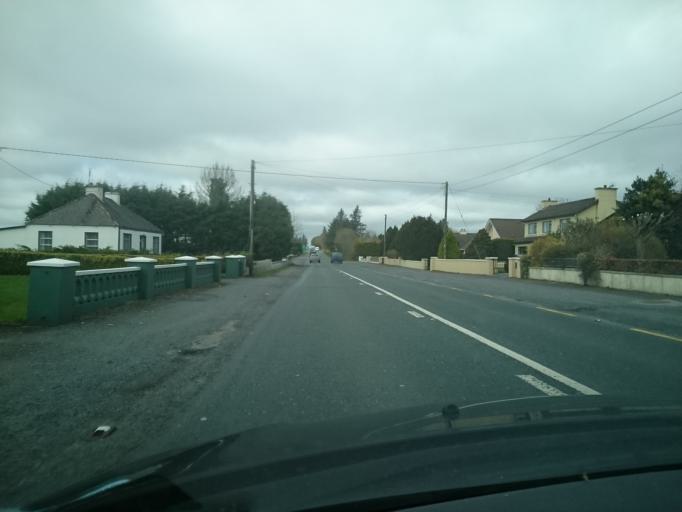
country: IE
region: Connaught
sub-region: Maigh Eo
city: Claremorris
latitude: 53.7388
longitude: -9.0100
